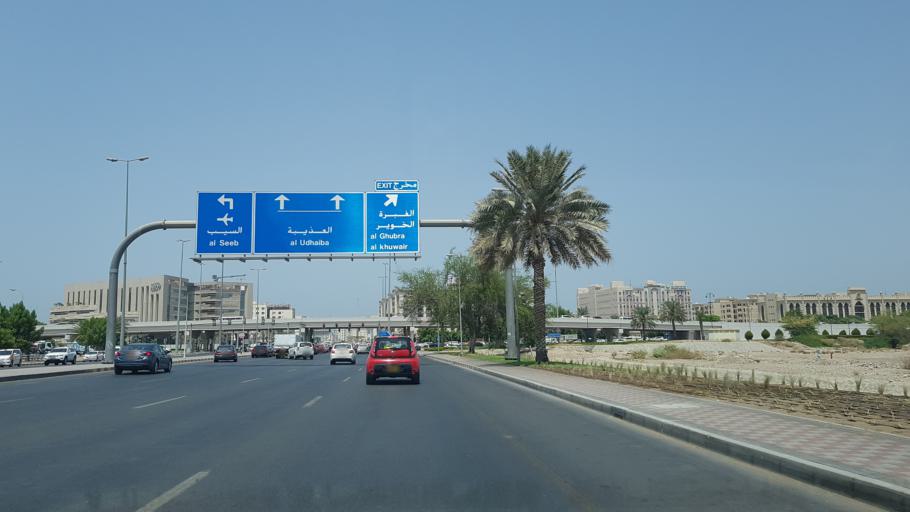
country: OM
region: Muhafazat Masqat
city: Bawshar
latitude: 23.5862
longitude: 58.3823
